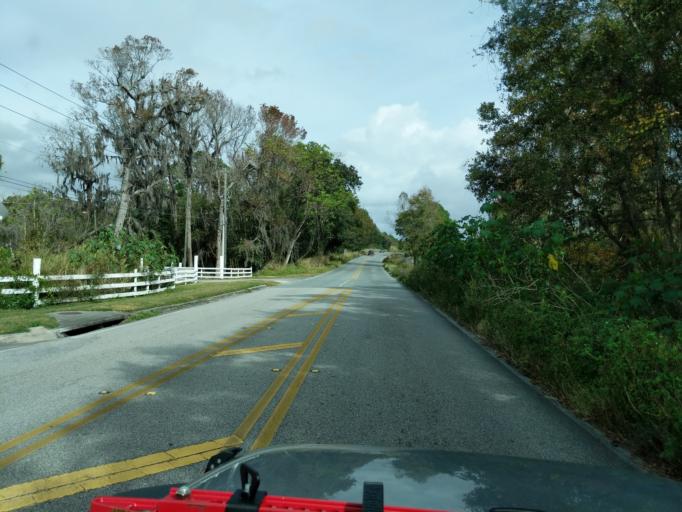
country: US
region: Florida
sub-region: Orange County
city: Ocoee
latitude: 28.5922
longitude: -81.5592
